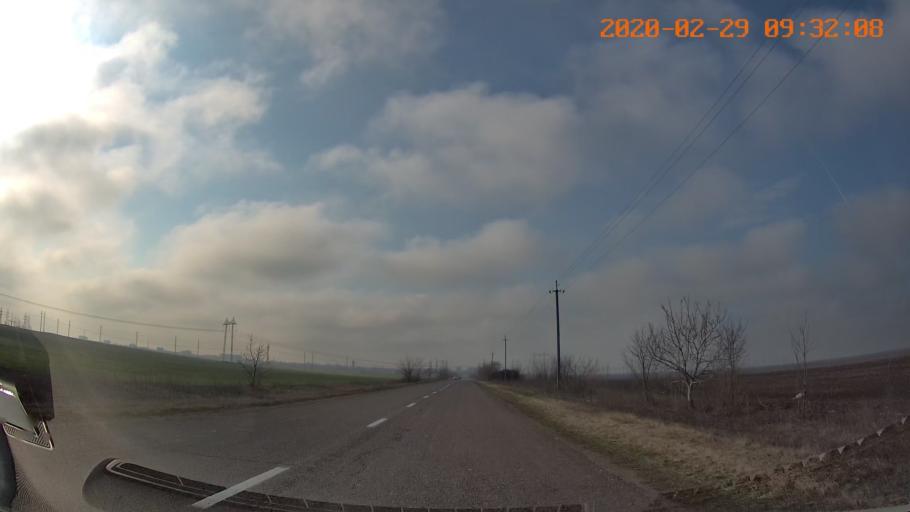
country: MD
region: Telenesti
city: Dnestrovsc
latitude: 46.6435
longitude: 29.9076
